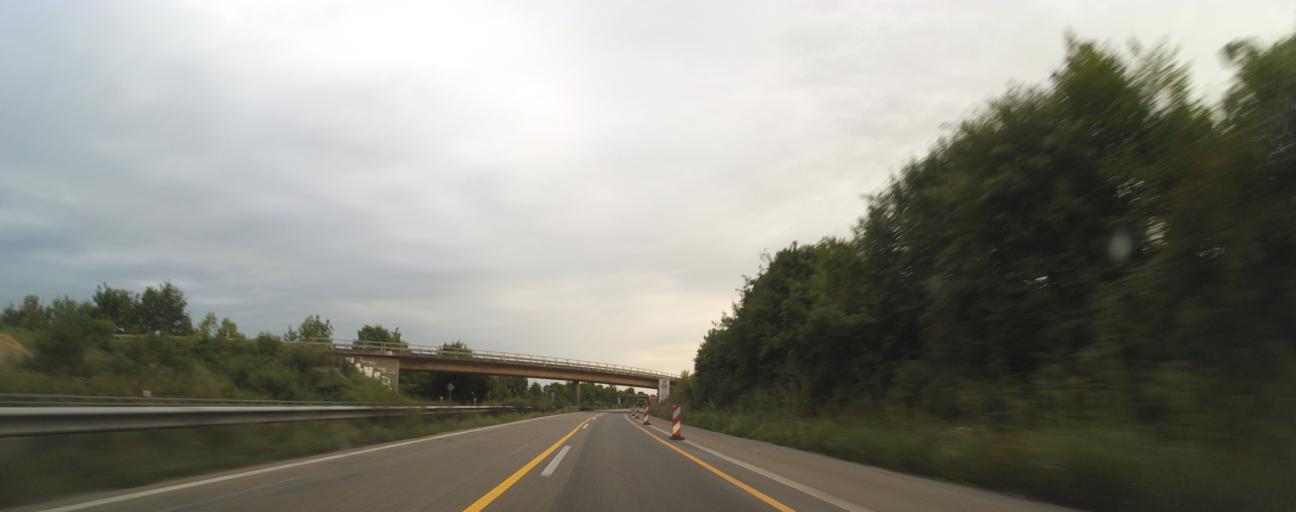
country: DE
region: Rheinland-Pfalz
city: Knoringen
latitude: 49.2263
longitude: 8.1477
